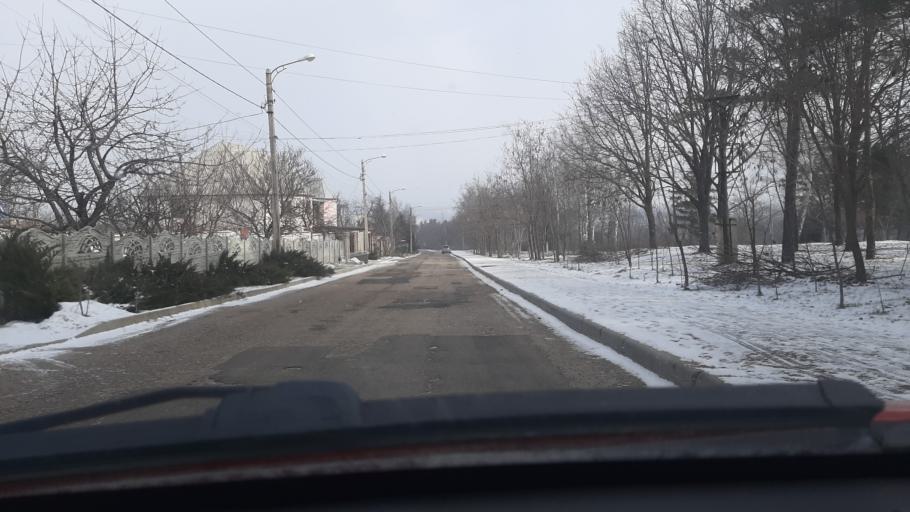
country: MD
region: Chisinau
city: Chisinau
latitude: 47.0057
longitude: 28.8070
